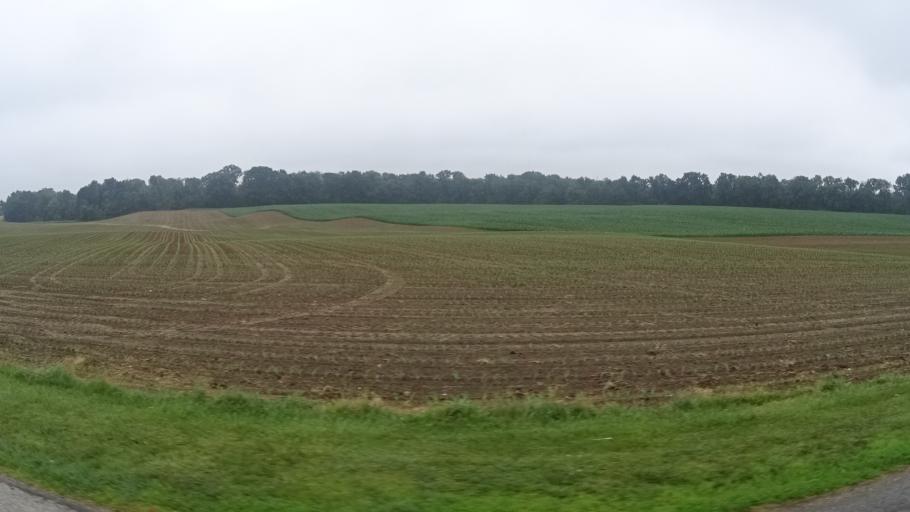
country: US
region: Ohio
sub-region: Erie County
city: Milan
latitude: 41.3442
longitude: -82.6137
